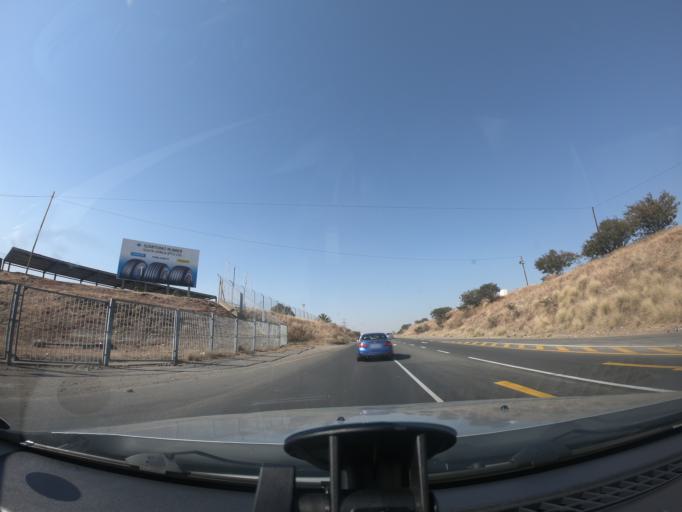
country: ZA
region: KwaZulu-Natal
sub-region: uThukela District Municipality
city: Ladysmith
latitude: -28.5494
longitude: 29.8297
